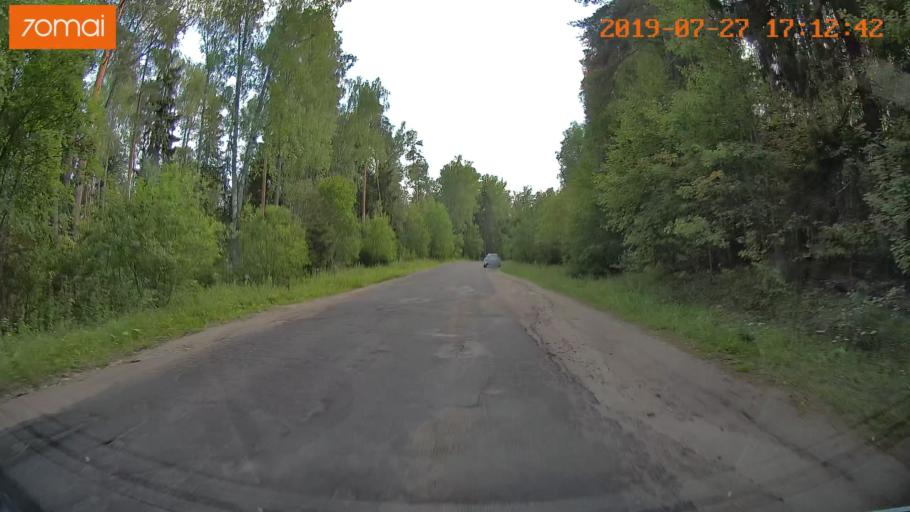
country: RU
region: Ivanovo
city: Novo-Talitsy
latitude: 57.0563
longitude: 40.8596
